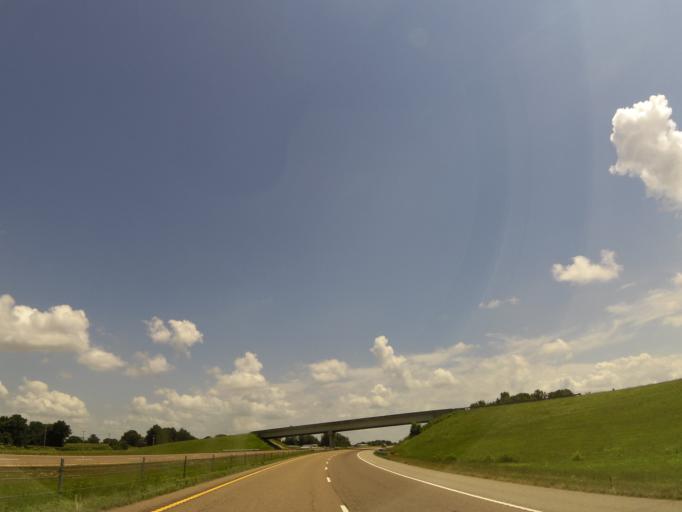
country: US
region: Tennessee
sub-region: Crockett County
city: Alamo
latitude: 35.8137
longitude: -89.1619
